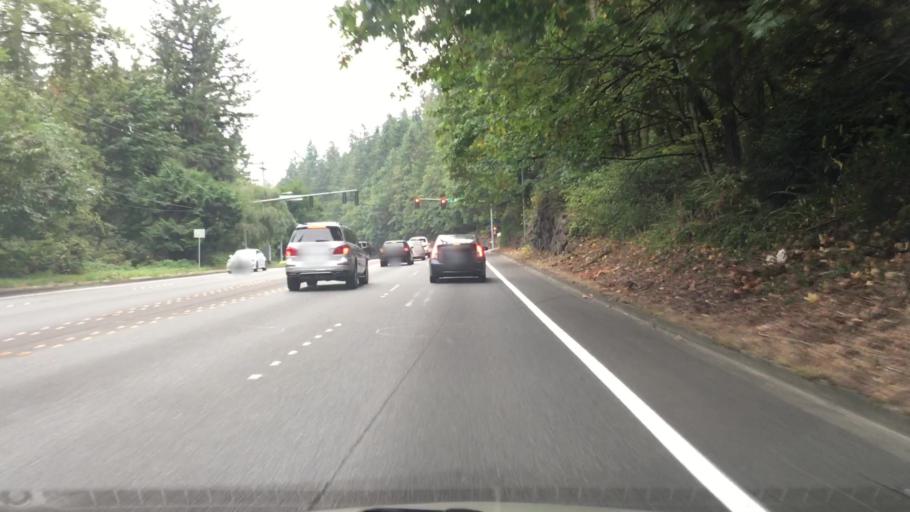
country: US
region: Washington
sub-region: King County
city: Newcastle
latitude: 47.5485
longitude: -122.1664
